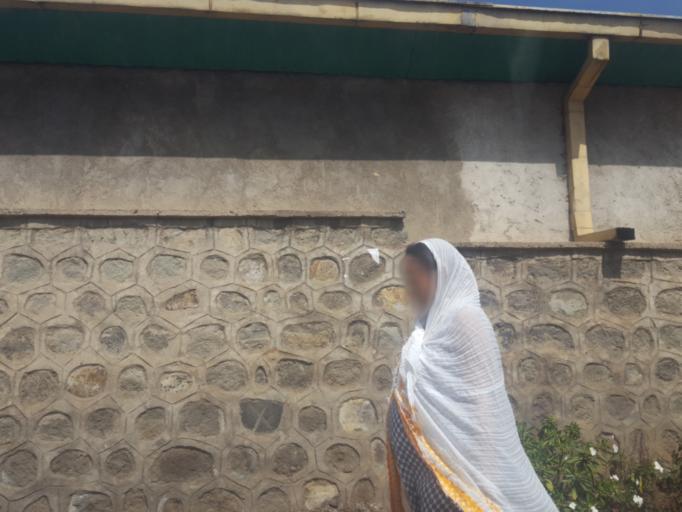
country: ET
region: Adis Abeba
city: Addis Ababa
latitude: 9.0572
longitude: 38.7280
